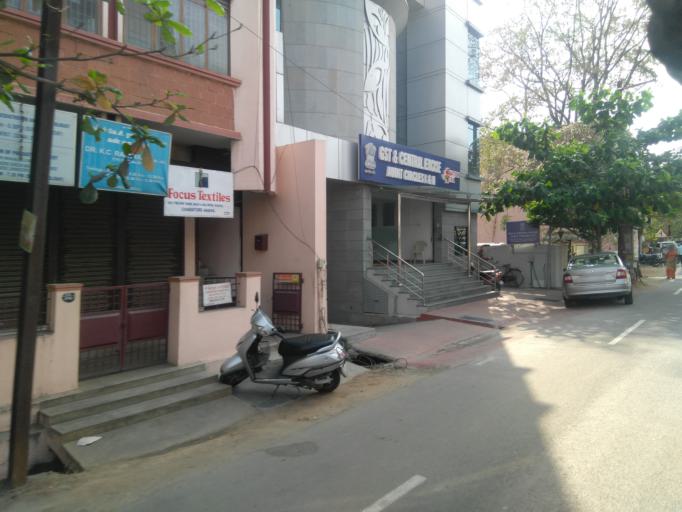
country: IN
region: Tamil Nadu
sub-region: Coimbatore
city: Coimbatore
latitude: 10.9979
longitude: 76.9894
